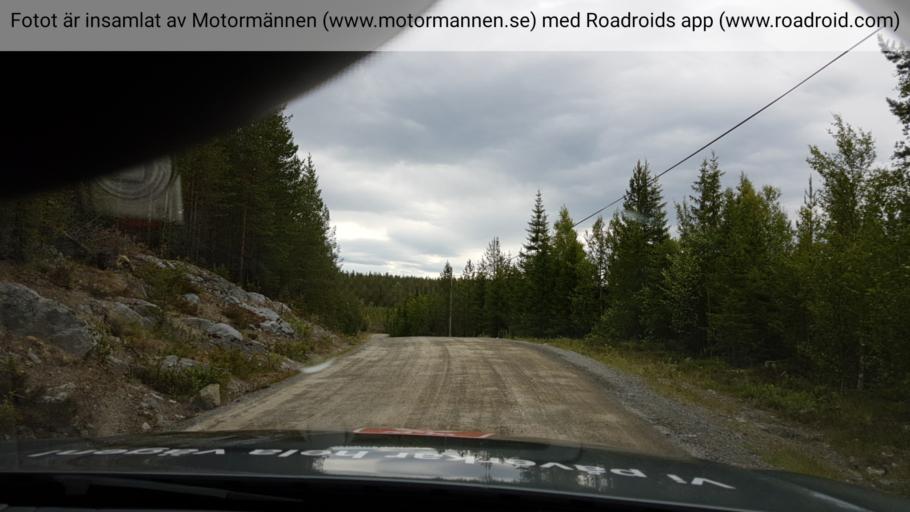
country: SE
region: Jaemtland
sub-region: Bergs Kommun
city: Hoverberg
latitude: 62.7900
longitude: 13.8202
